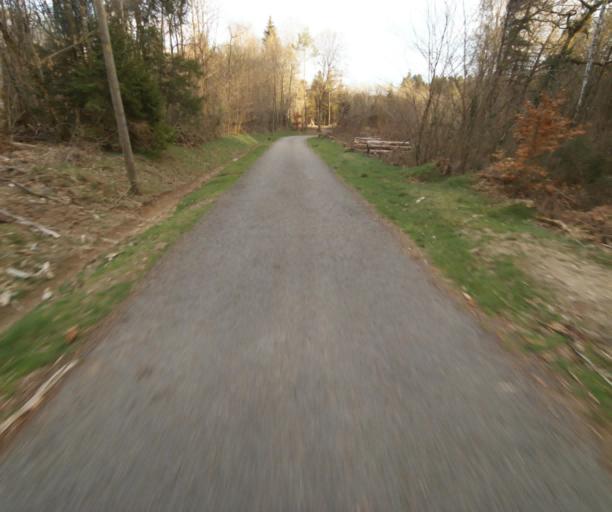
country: FR
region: Limousin
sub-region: Departement de la Correze
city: Argentat
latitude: 45.2301
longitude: 1.9674
